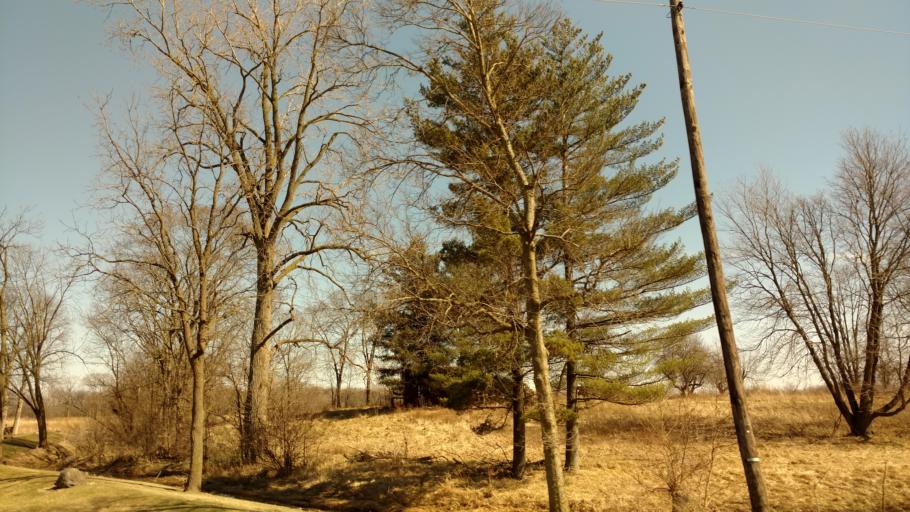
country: US
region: Ohio
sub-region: Union County
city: Richwood
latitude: 40.5158
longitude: -83.3426
